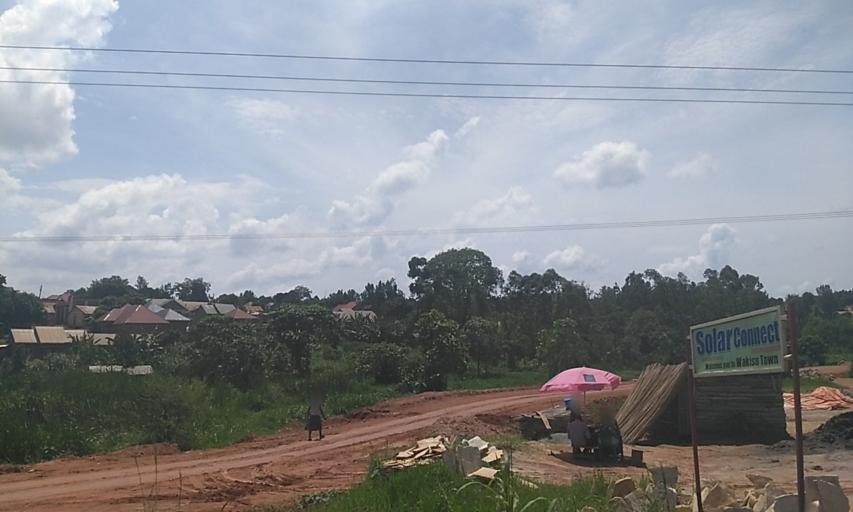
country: UG
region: Central Region
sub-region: Wakiso District
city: Wakiso
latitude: 0.3975
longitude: 32.4843
